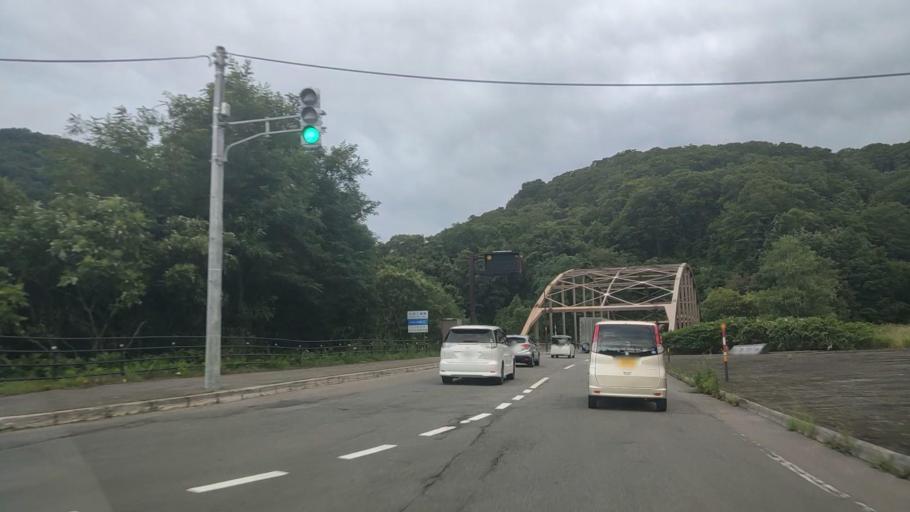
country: JP
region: Hokkaido
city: Nanae
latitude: 41.9564
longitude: 140.6504
